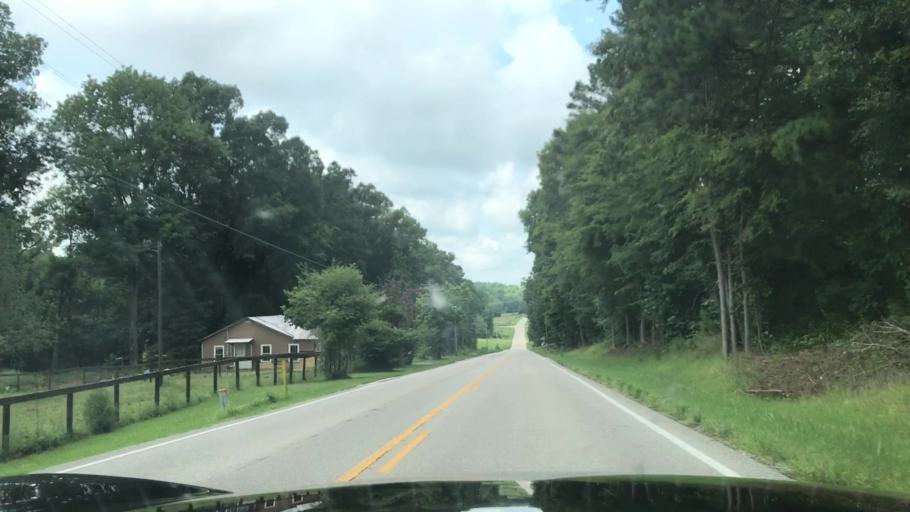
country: US
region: Kentucky
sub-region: Butler County
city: Morgantown
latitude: 37.1733
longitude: -86.8122
